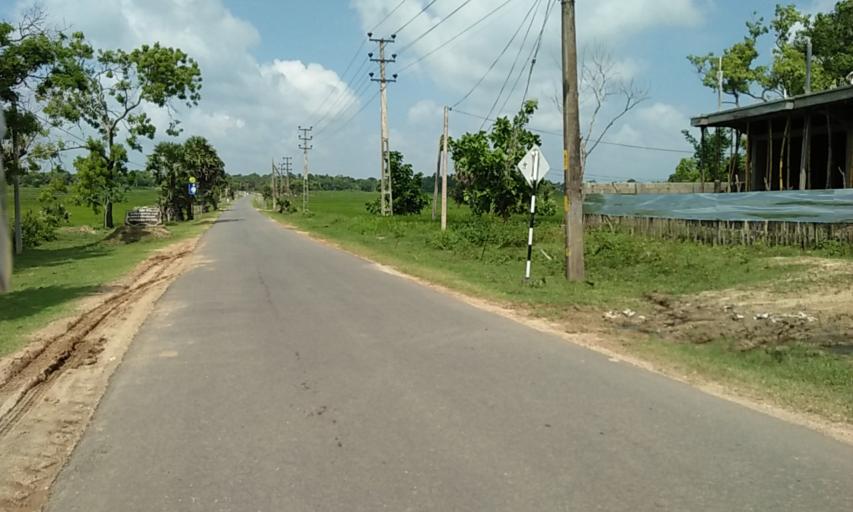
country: LK
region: Eastern Province
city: Ampara
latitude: 7.3383
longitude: 81.7425
